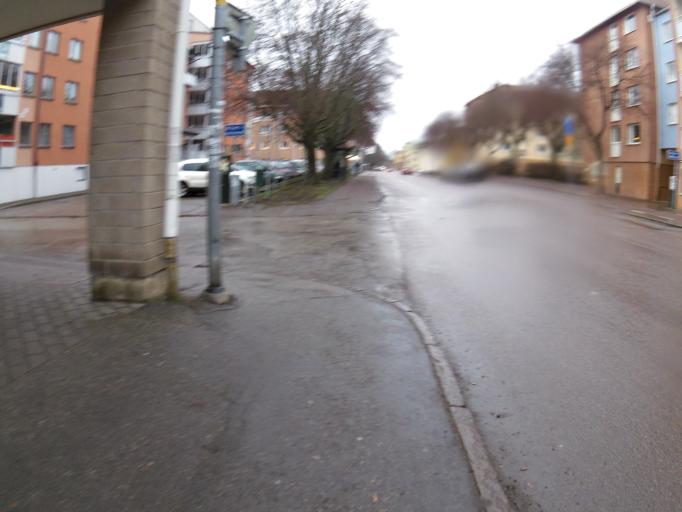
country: SE
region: Gaevleborg
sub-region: Gavle Kommun
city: Gavle
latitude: 60.6698
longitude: 17.1466
